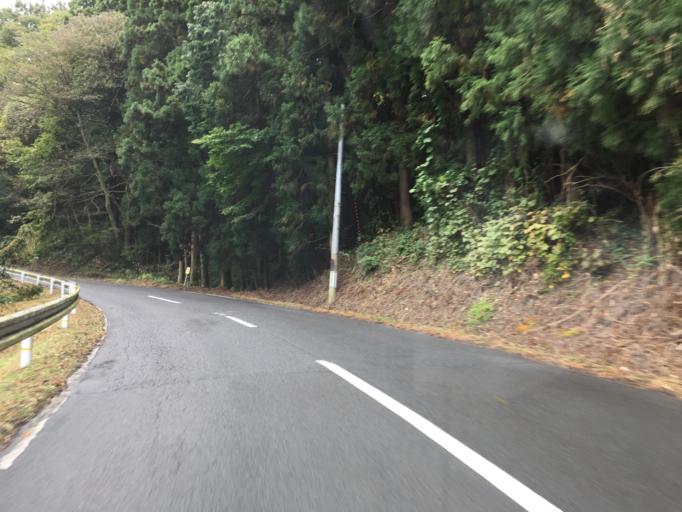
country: JP
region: Fukushima
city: Nihommatsu
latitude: 37.6298
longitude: 140.4374
